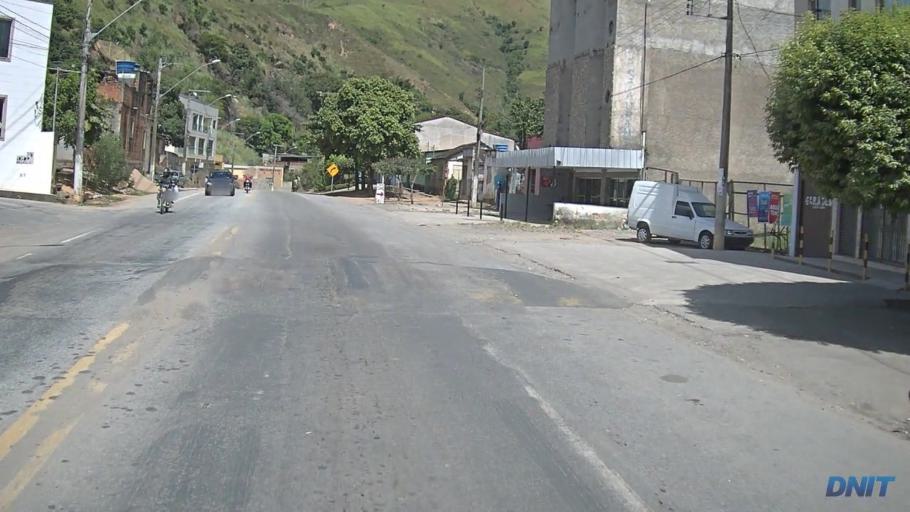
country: BR
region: Minas Gerais
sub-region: Coronel Fabriciano
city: Coronel Fabriciano
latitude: -19.5335
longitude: -42.6680
